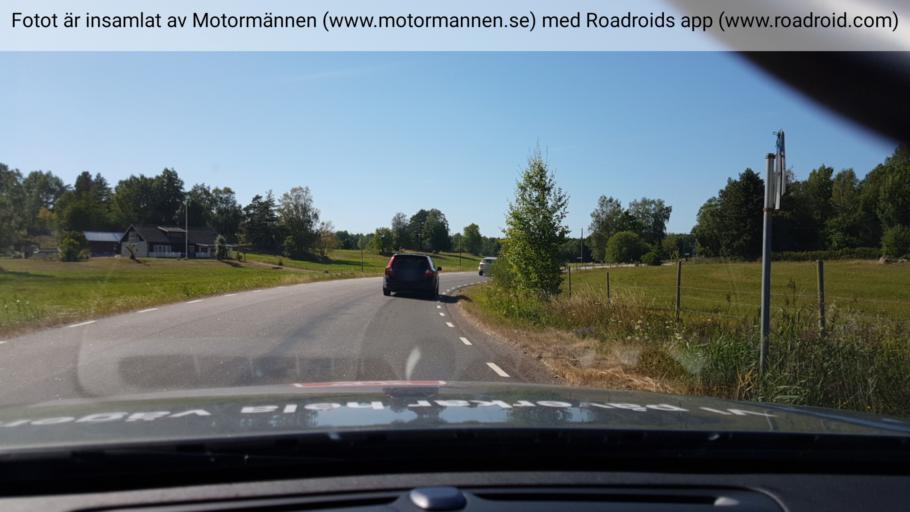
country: SE
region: Vaestra Goetaland
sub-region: Toreboda Kommun
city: Toereboda
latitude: 58.6833
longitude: 14.2074
